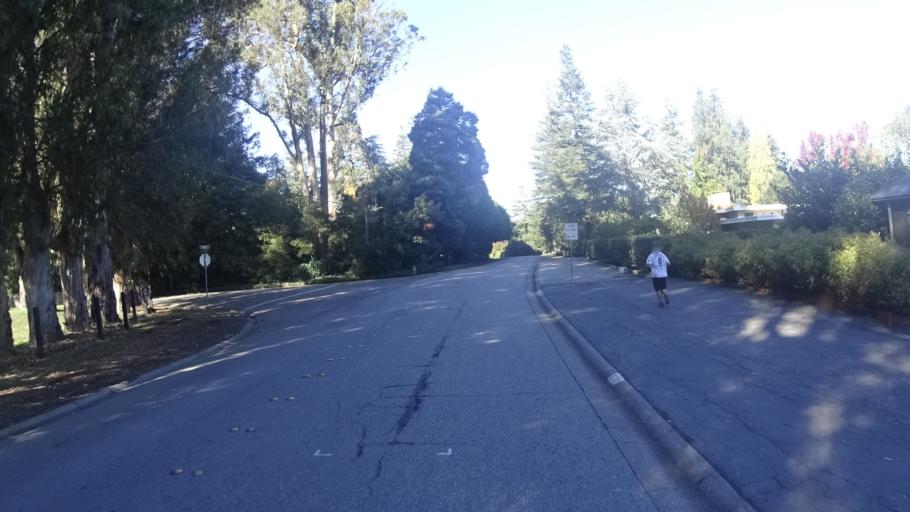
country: US
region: California
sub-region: San Mateo County
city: Burlingame
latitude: 37.5754
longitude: -122.3594
